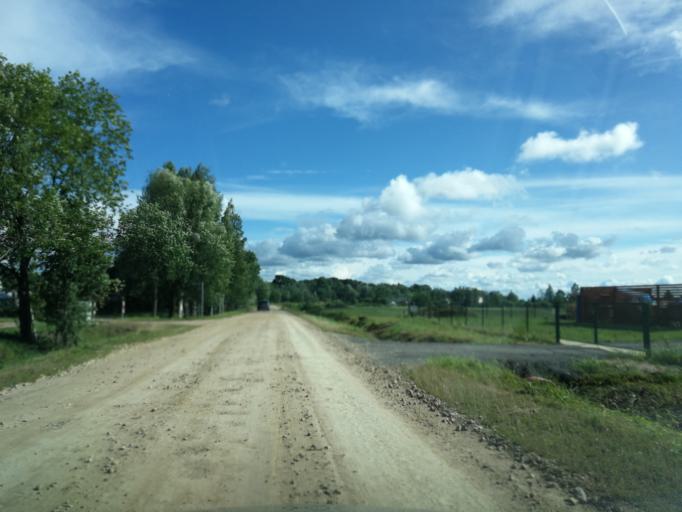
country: LV
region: Adazi
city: Adazi
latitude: 57.0975
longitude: 24.3236
